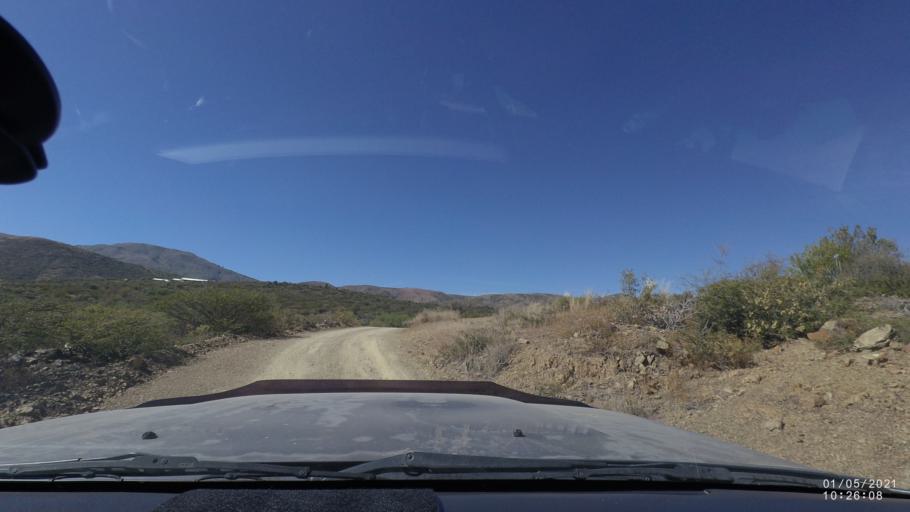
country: BO
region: Cochabamba
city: Capinota
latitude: -17.5807
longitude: -66.1926
